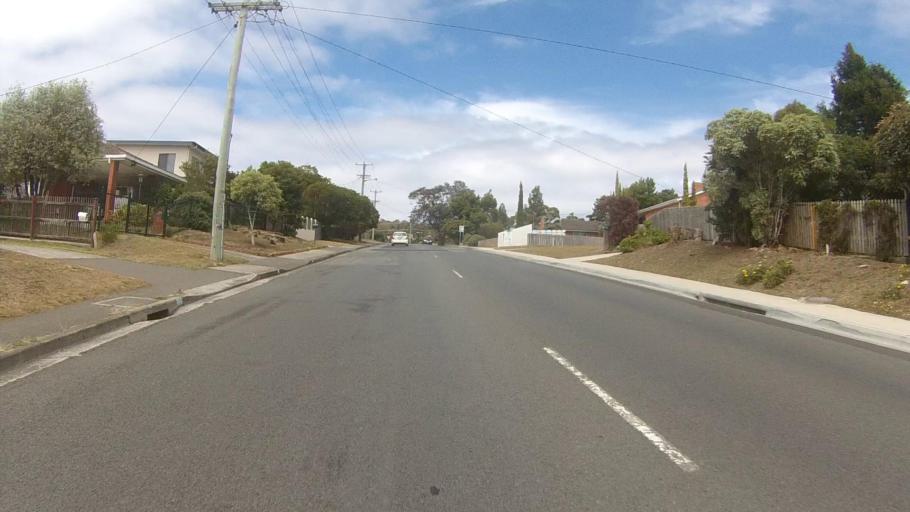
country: AU
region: Tasmania
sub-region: Kingborough
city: Blackmans Bay
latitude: -43.0046
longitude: 147.3191
